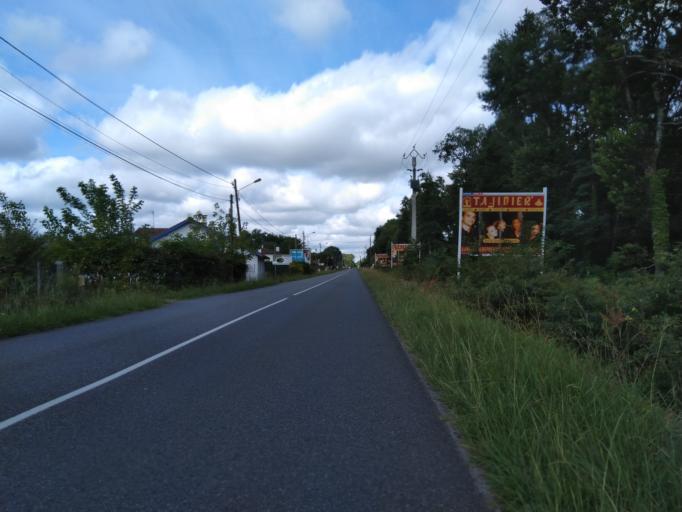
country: FR
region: Aquitaine
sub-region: Departement des Landes
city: Mees
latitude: 43.7305
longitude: -1.0944
